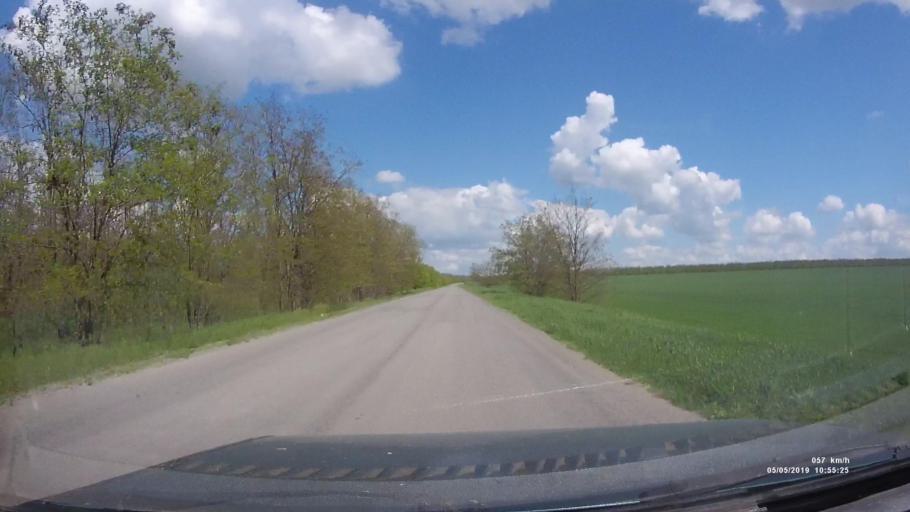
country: RU
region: Rostov
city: Ust'-Donetskiy
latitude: 47.6654
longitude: 40.8212
